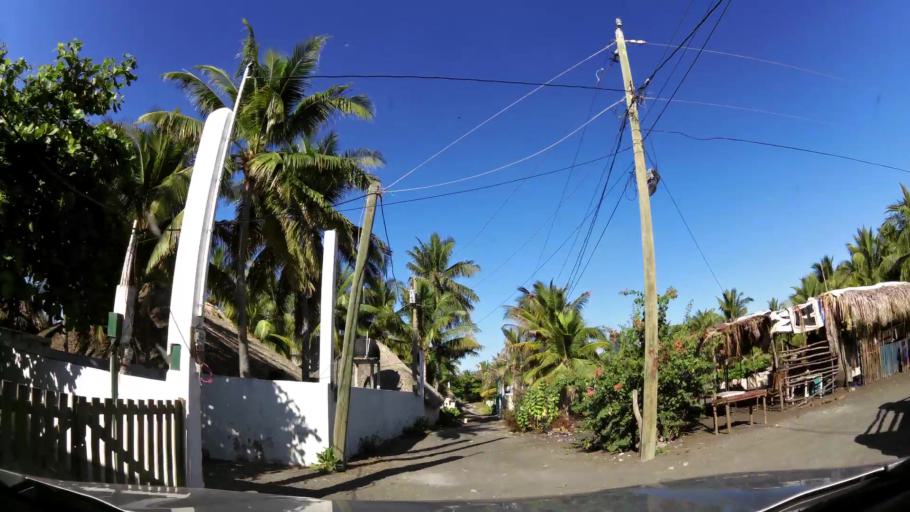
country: GT
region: Santa Rosa
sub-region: Municipio de Taxisco
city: Taxisco
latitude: 13.8926
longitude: -90.4910
